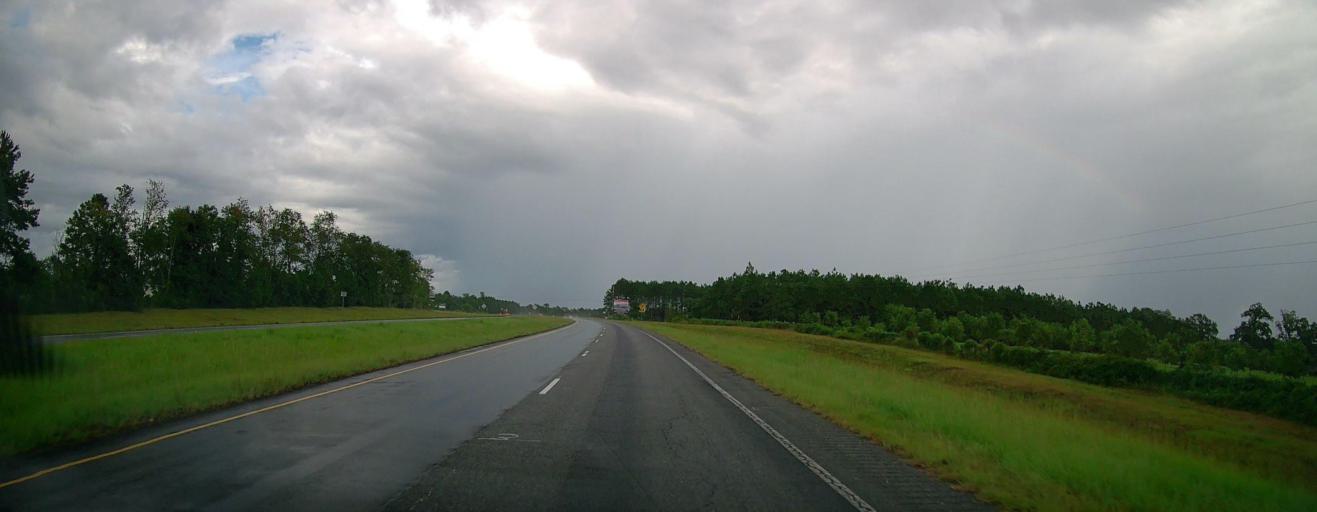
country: US
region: Georgia
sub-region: Ware County
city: Deenwood
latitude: 31.2543
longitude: -82.4746
